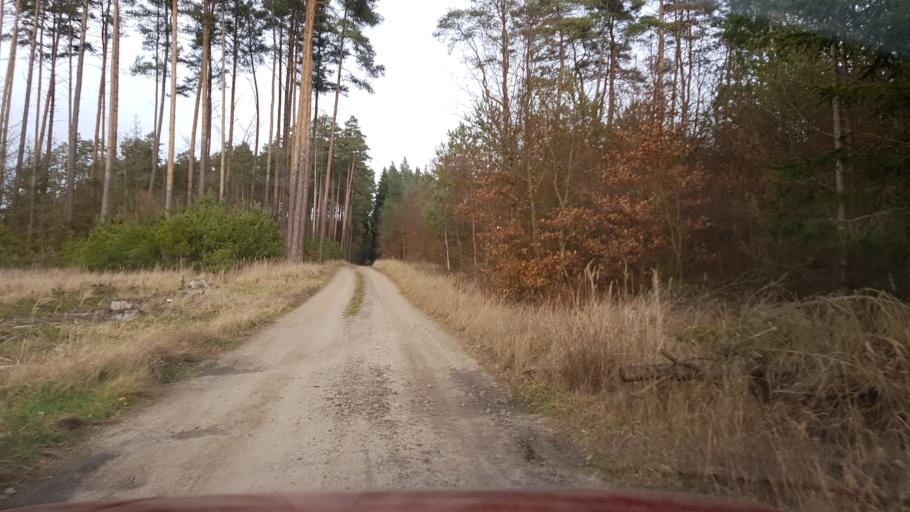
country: PL
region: Lubusz
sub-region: Powiat strzelecko-drezdenecki
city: Strzelce Krajenskie
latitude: 52.9072
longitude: 15.4069
